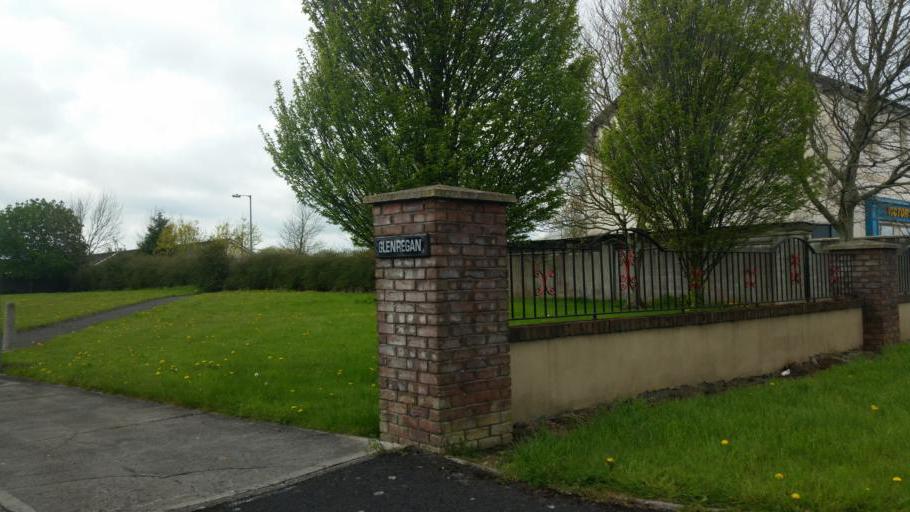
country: IE
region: Leinster
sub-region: Laois
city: Portlaoise
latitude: 53.0430
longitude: -7.3115
